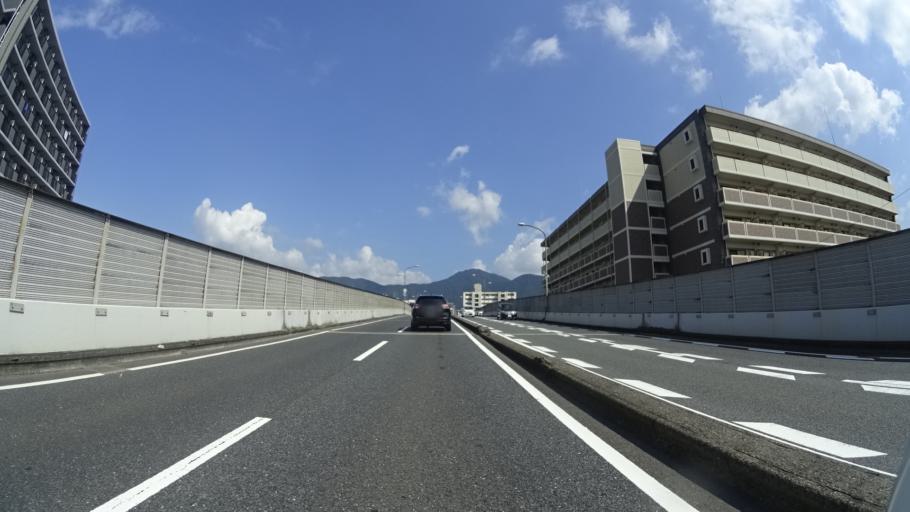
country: JP
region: Fukuoka
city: Kitakyushu
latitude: 33.8652
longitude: 130.8753
